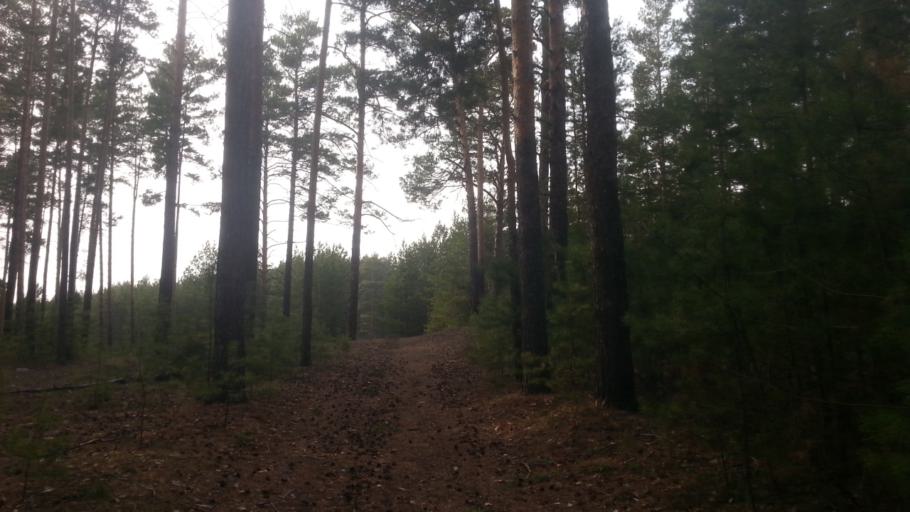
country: RU
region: Altai Krai
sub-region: Gorod Barnaulskiy
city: Barnaul
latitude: 53.3244
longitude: 83.7165
